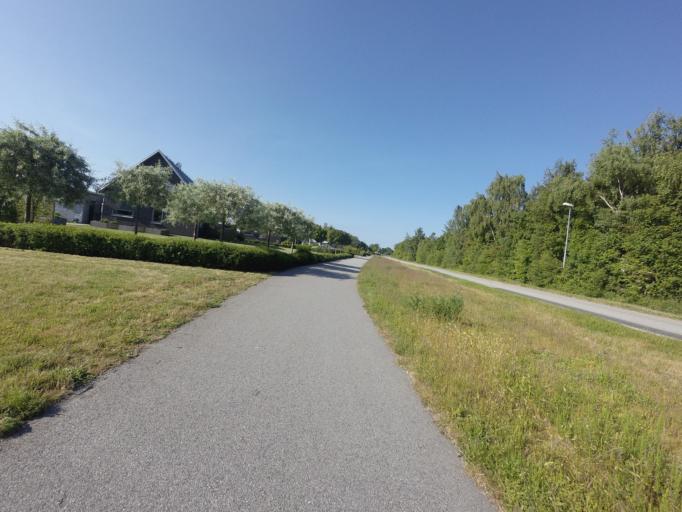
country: SE
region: Skane
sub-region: Vellinge Kommun
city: Hollviken
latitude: 55.4082
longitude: 13.0034
